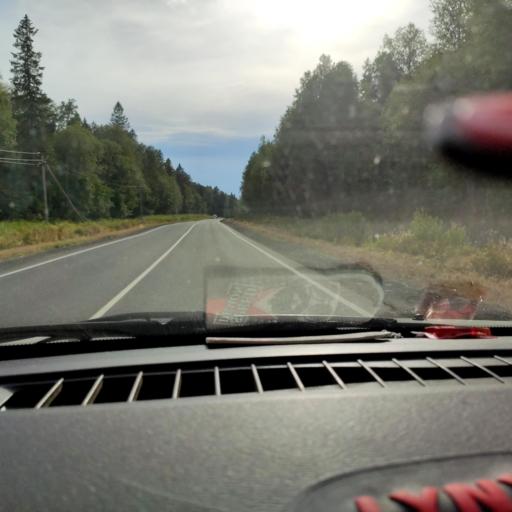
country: RU
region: Perm
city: Perm
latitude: 58.1945
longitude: 56.2518
